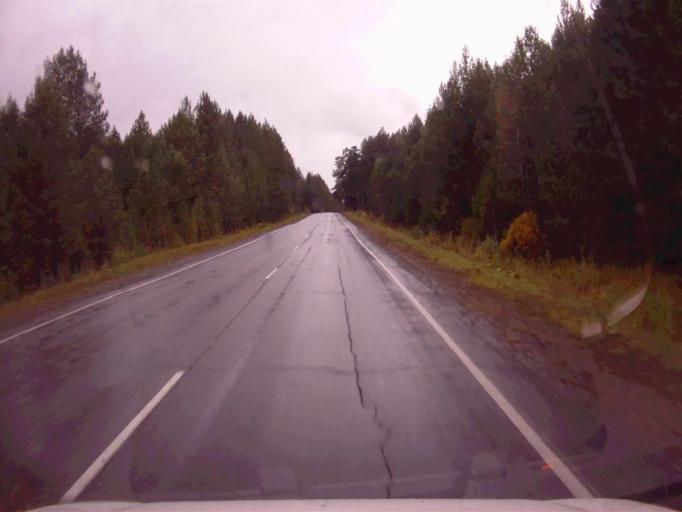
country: RU
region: Chelyabinsk
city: Verkhniy Ufaley
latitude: 56.0200
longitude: 60.3038
